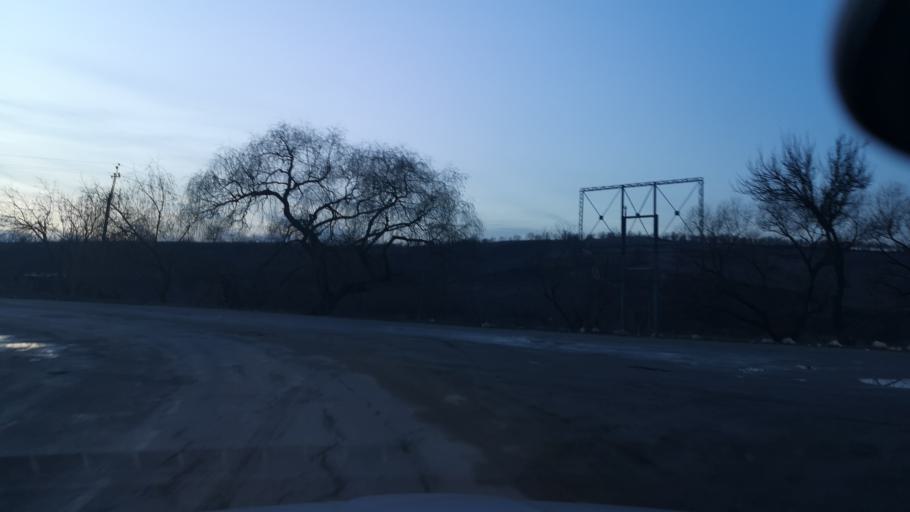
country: MD
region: Orhei
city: Orhei
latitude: 47.3096
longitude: 28.9320
